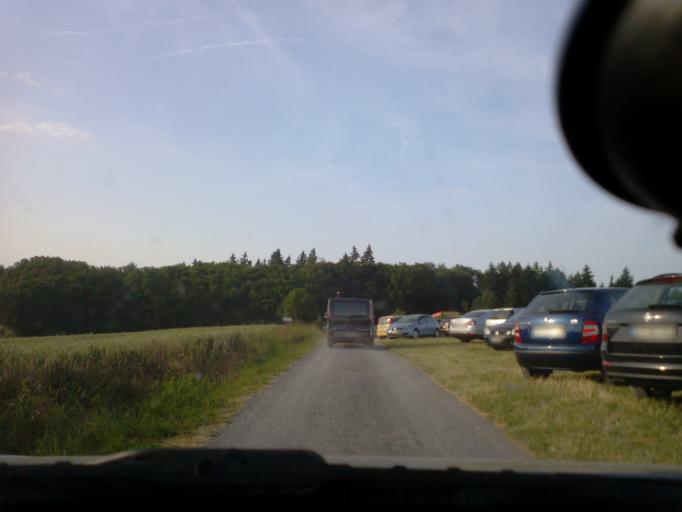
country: DE
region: Baden-Wuerttemberg
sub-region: Karlsruhe Region
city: Bretten
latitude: 48.9917
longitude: 8.7051
